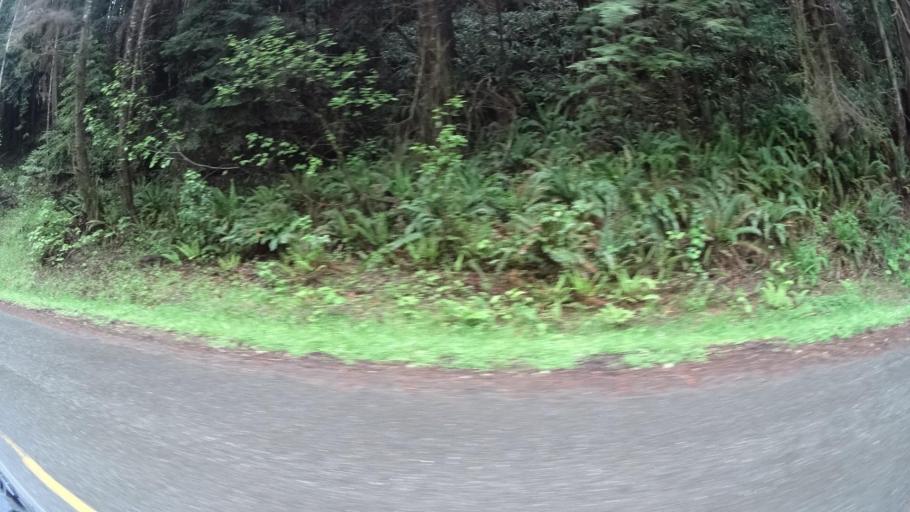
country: US
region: California
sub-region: Humboldt County
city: Bayside
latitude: 40.8178
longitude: -124.0288
